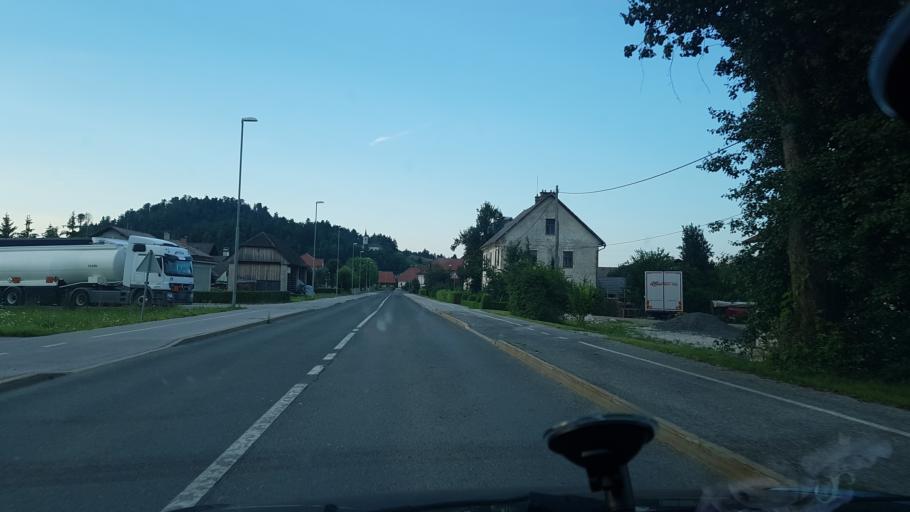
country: SI
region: Logatec
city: Logatec
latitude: 45.9068
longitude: 14.2021
